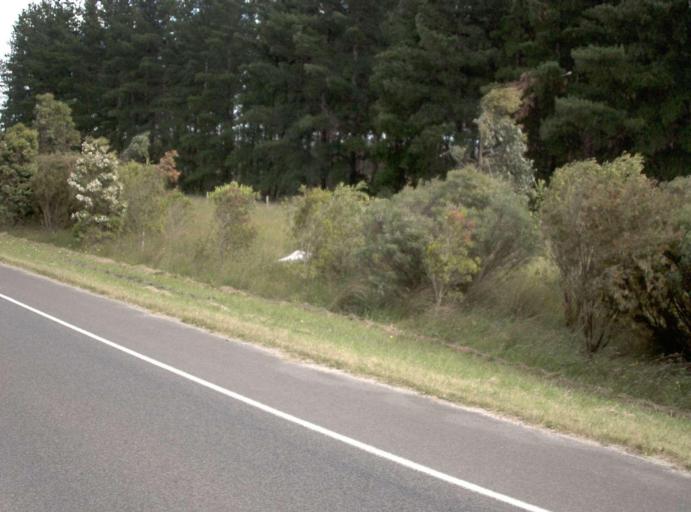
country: AU
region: Victoria
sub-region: Latrobe
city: Traralgon
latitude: -38.1870
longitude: 146.4631
